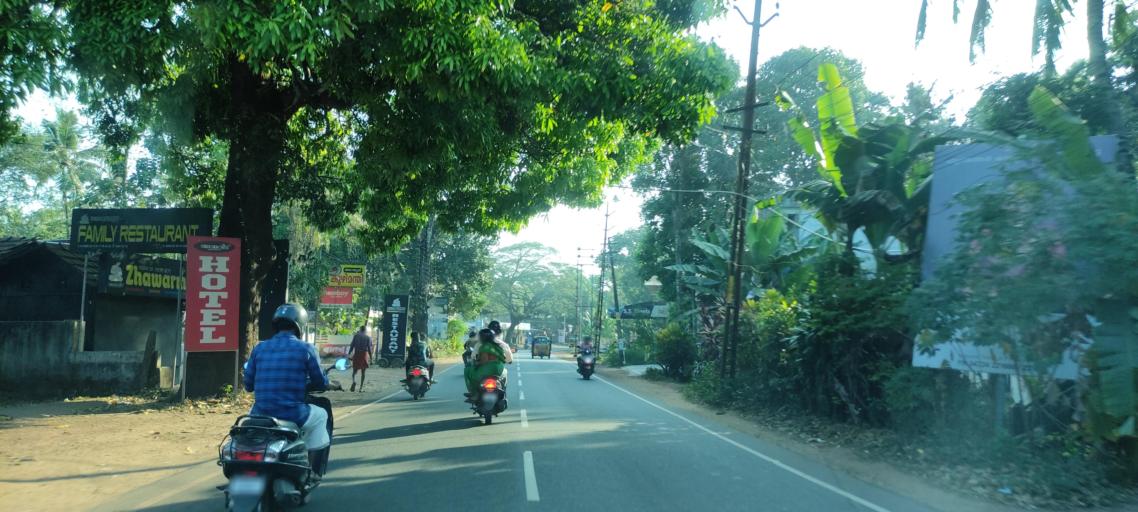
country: IN
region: Kerala
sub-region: Alappuzha
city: Kattanam
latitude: 9.1754
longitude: 76.6139
